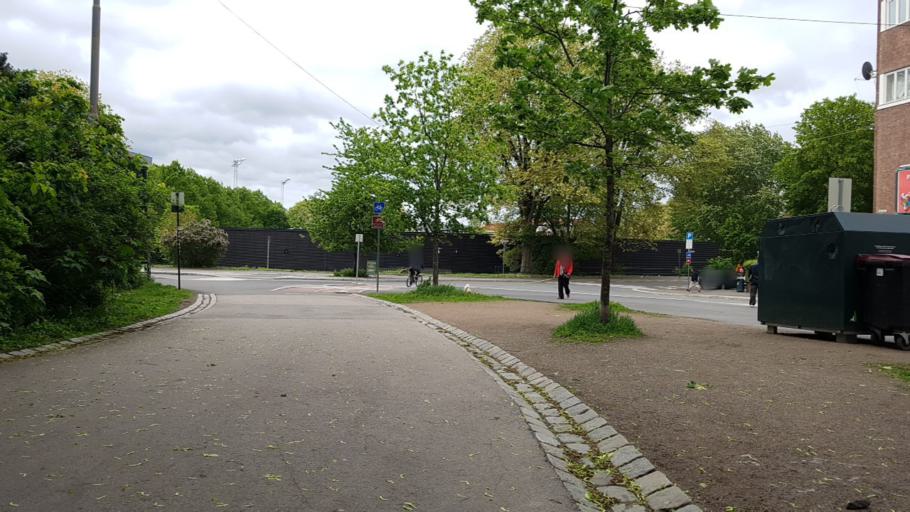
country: NO
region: Oslo
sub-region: Oslo
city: Oslo
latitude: 59.9275
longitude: 10.7663
